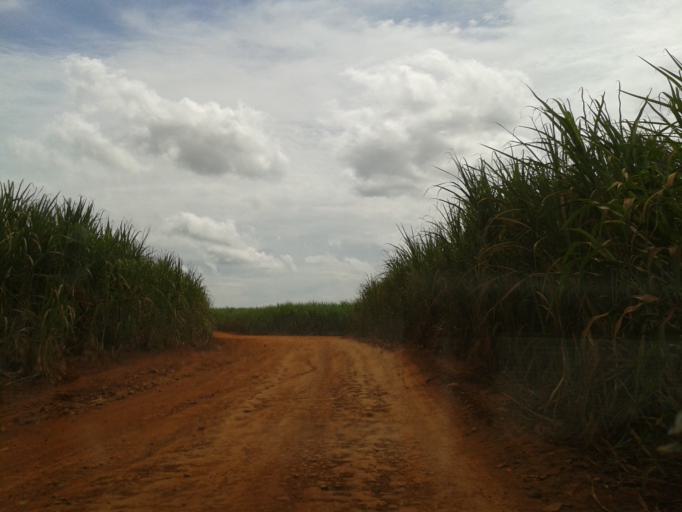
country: BR
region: Minas Gerais
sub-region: Centralina
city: Centralina
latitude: -18.7673
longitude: -49.2559
